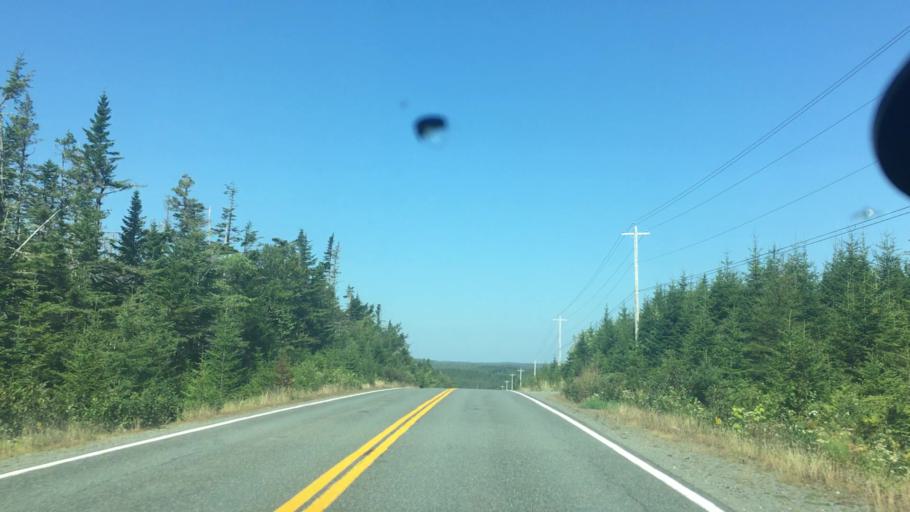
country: CA
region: Nova Scotia
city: Antigonish
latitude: 44.9914
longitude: -62.0964
